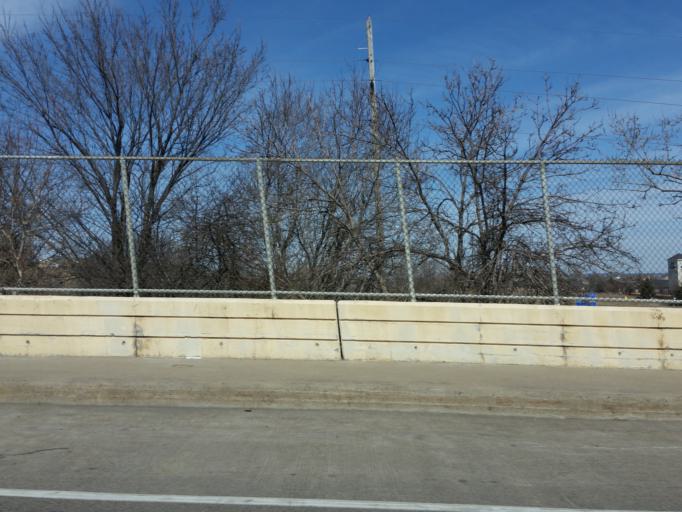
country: US
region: Minnesota
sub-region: Dakota County
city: Eagan
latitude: 44.7903
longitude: -93.2221
